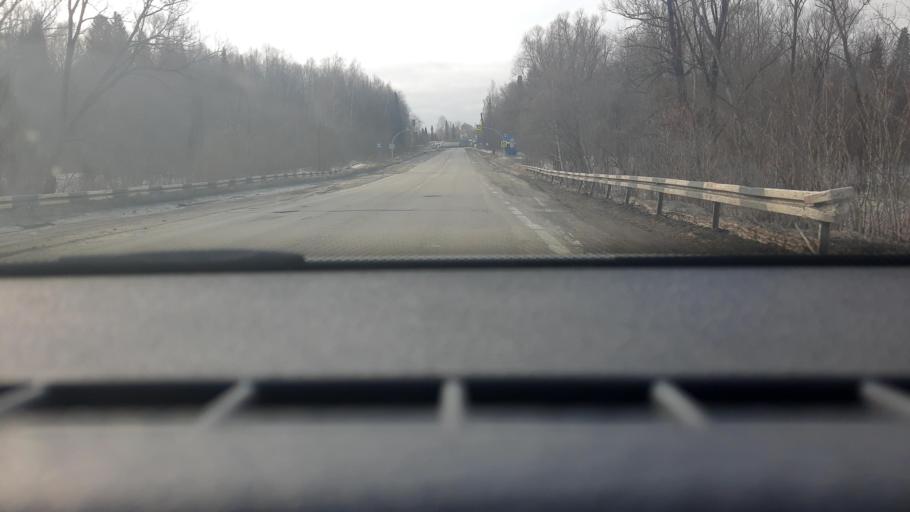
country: RU
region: Chelyabinsk
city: Asha
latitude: 54.8920
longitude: 57.2996
